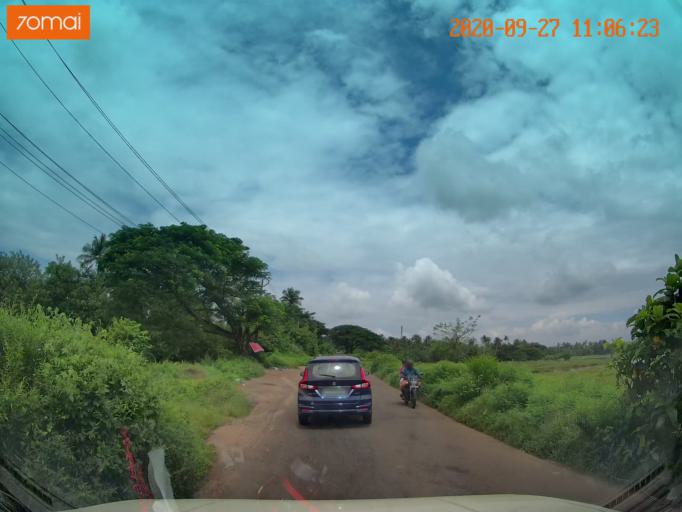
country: IN
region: Kerala
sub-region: Thrissur District
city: Irinjalakuda
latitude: 10.4253
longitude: 76.2423
